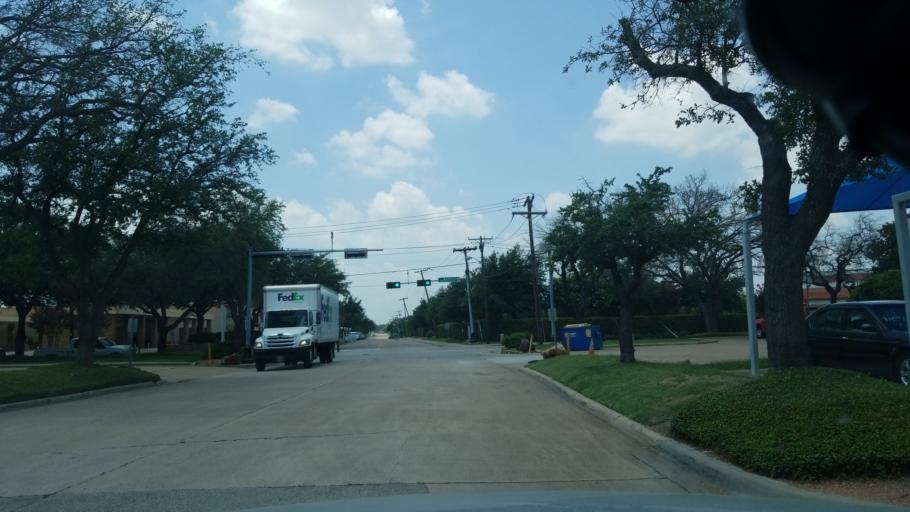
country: US
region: Texas
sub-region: Dallas County
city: Carrollton
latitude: 32.9608
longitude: -96.8766
